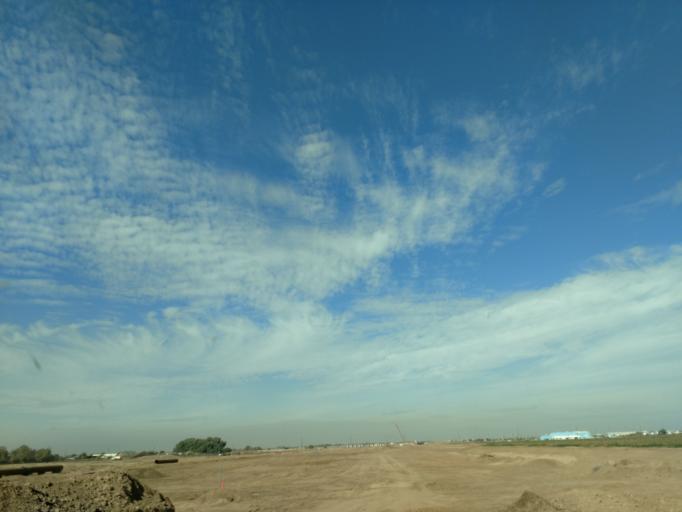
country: US
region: Arizona
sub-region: Maricopa County
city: Laveen
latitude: 33.3844
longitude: -112.1904
